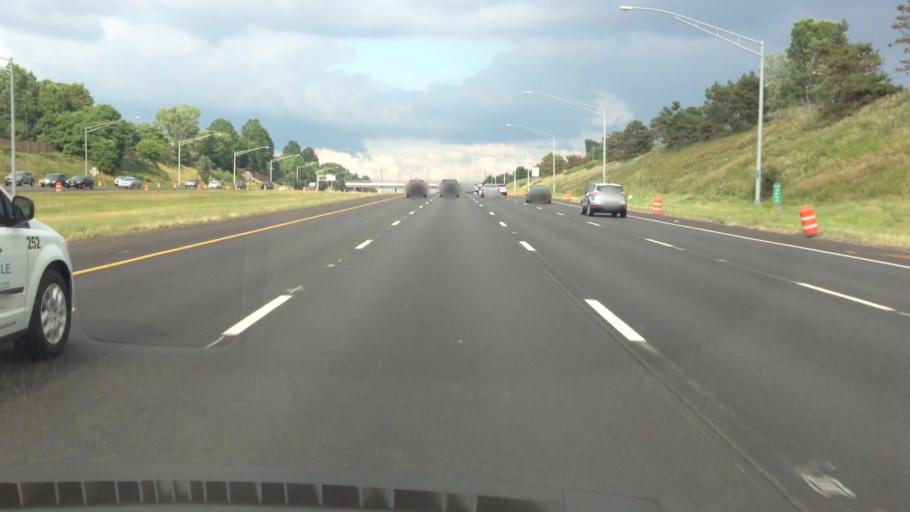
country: US
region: Ohio
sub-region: Cuyahoga County
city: Garfield Heights
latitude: 41.4122
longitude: -81.6109
